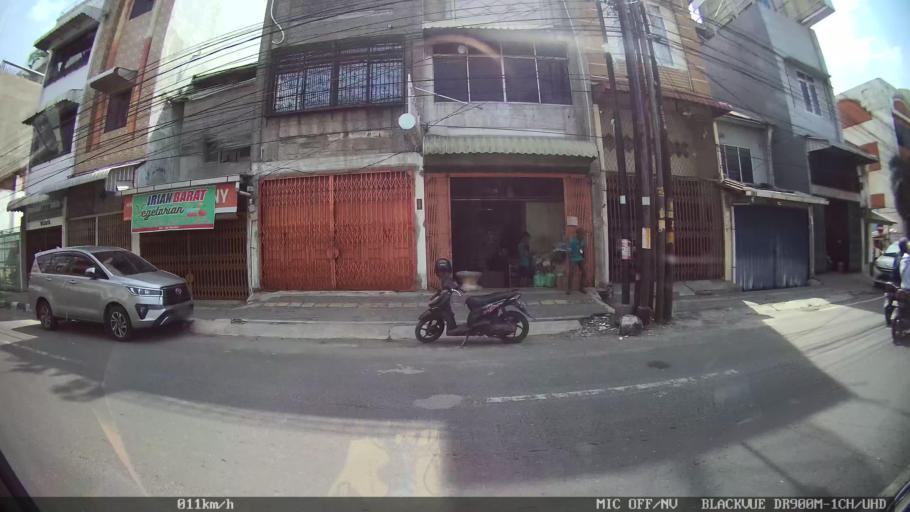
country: ID
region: North Sumatra
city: Medan
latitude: 3.5886
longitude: 98.6826
